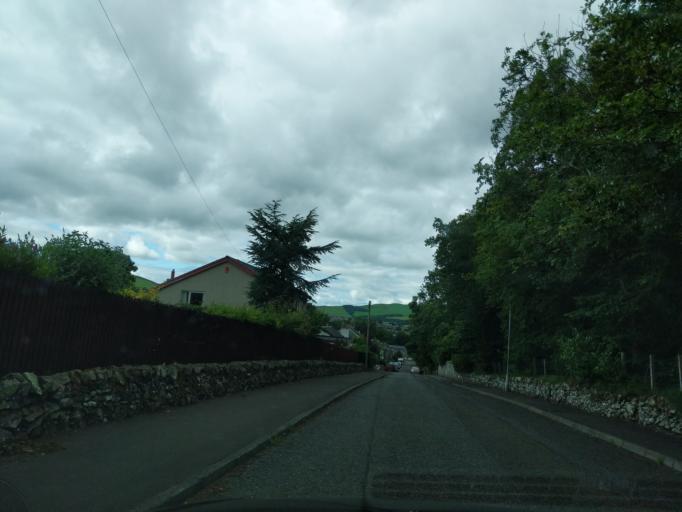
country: GB
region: Scotland
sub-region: The Scottish Borders
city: Peebles
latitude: 55.6461
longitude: -3.1992
